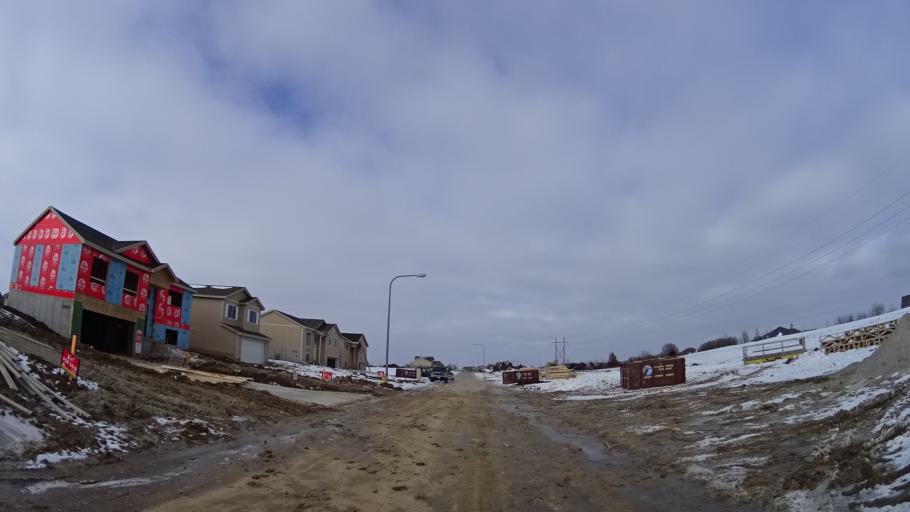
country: US
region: Nebraska
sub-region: Sarpy County
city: Offutt Air Force Base
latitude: 41.1040
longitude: -95.9768
